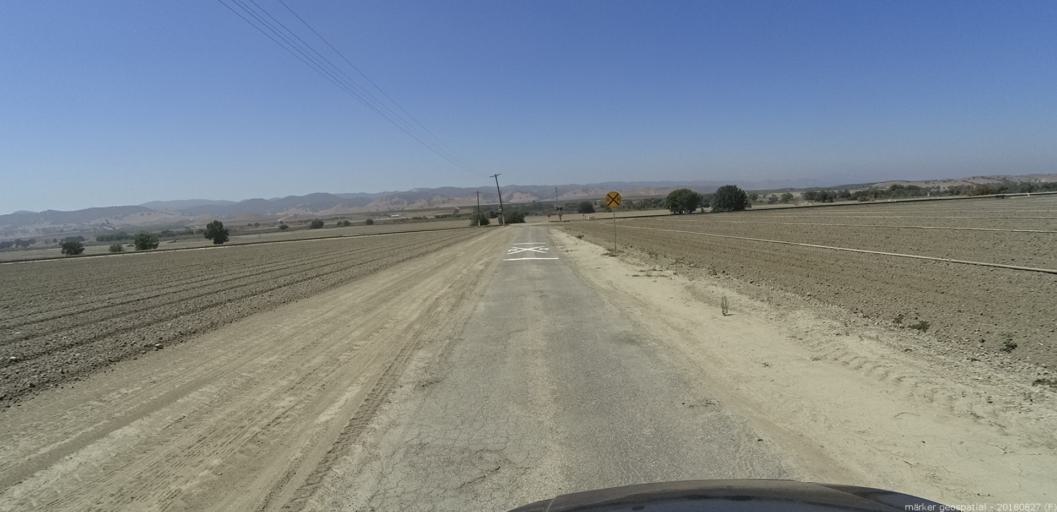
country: US
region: California
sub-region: Monterey County
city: King City
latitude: 36.0462
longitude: -120.9150
